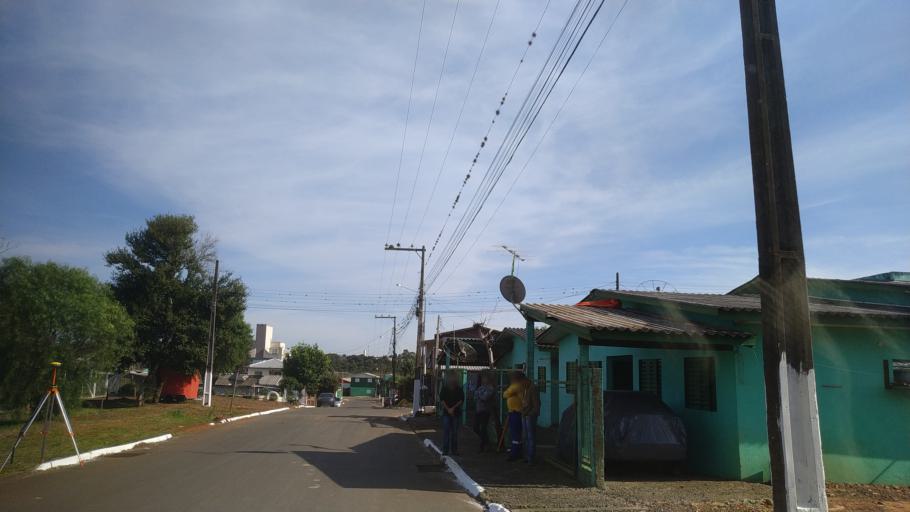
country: BR
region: Santa Catarina
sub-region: Chapeco
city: Chapeco
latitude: -27.1017
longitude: -52.6543
